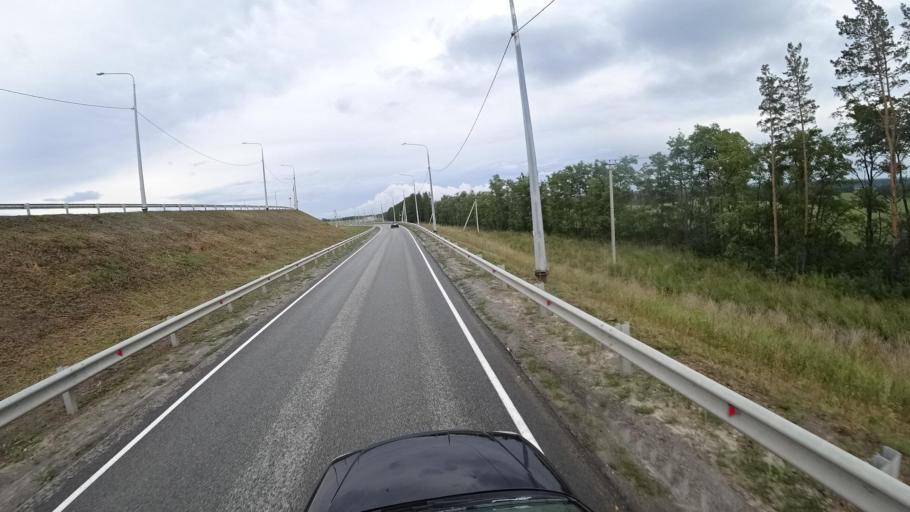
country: RU
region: Sverdlovsk
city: Kamyshlov
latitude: 56.8468
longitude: 62.8334
